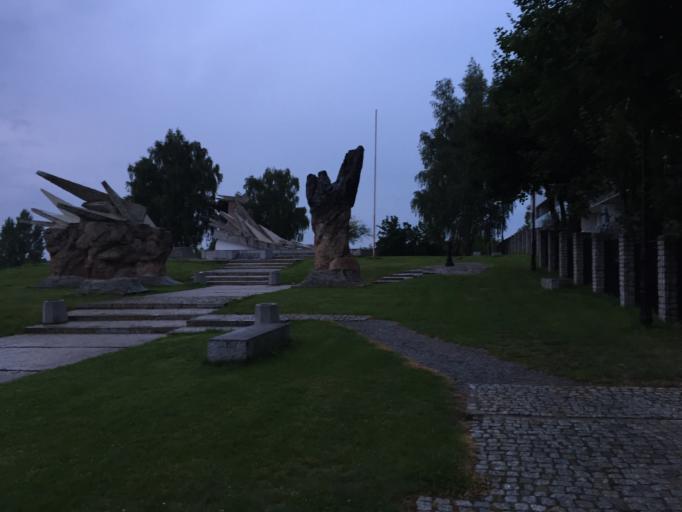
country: PL
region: Podlasie
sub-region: Bialystok
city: Bialystok
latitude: 53.1418
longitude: 23.0996
